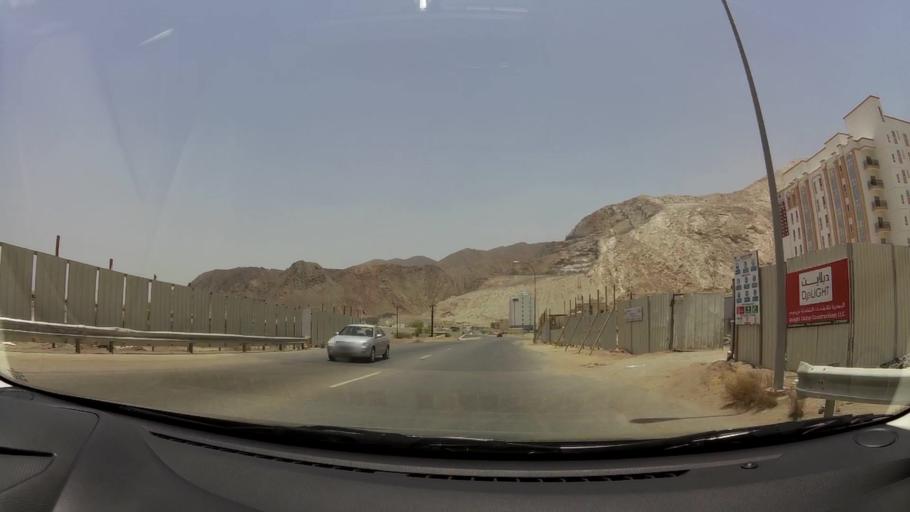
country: OM
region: Muhafazat Masqat
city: Bawshar
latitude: 23.5645
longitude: 58.4196
